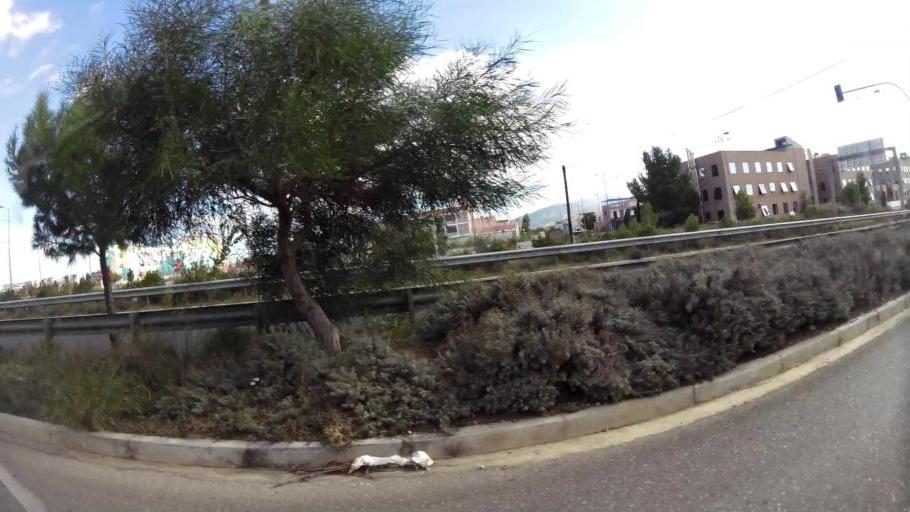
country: GR
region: Attica
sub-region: Nomarchia Anatolikis Attikis
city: Thrakomakedones
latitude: 38.1065
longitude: 23.7636
